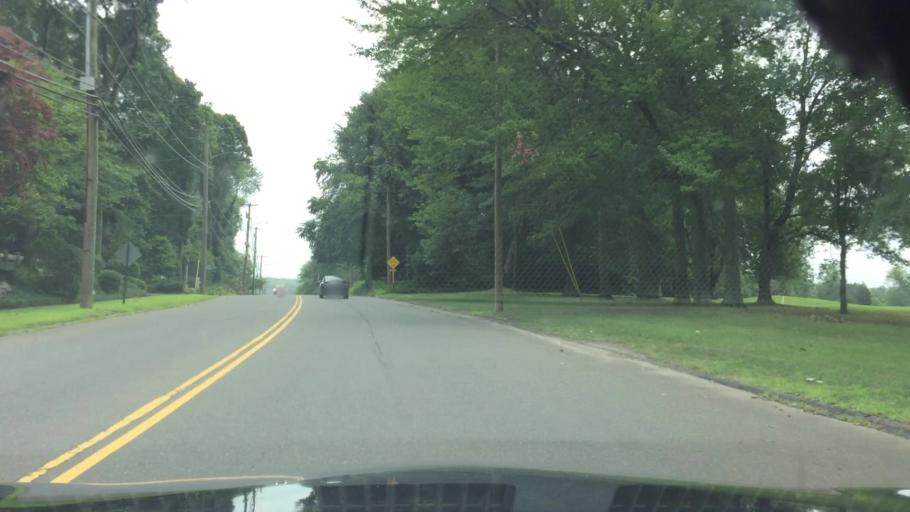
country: US
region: Connecticut
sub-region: New Haven County
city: City of Milford (balance)
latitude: 41.2499
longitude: -73.1091
